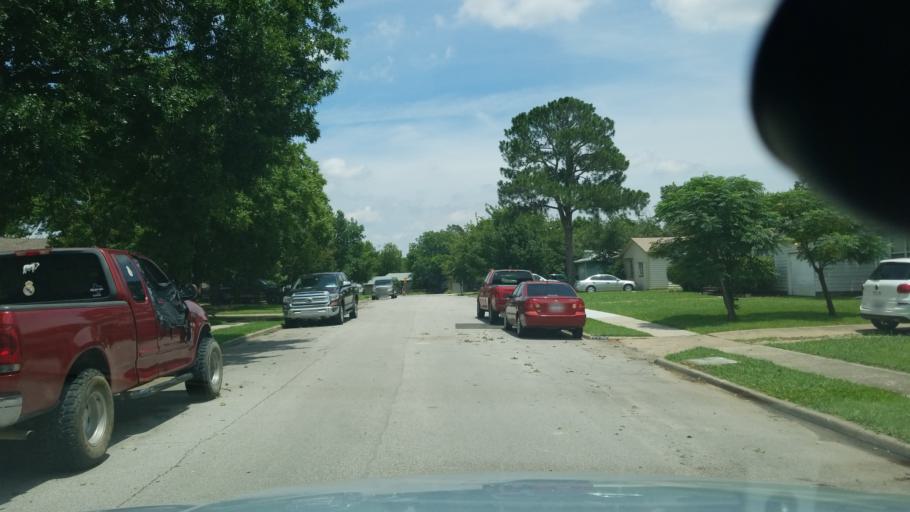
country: US
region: Texas
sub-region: Dallas County
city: Irving
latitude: 32.8441
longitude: -96.9740
